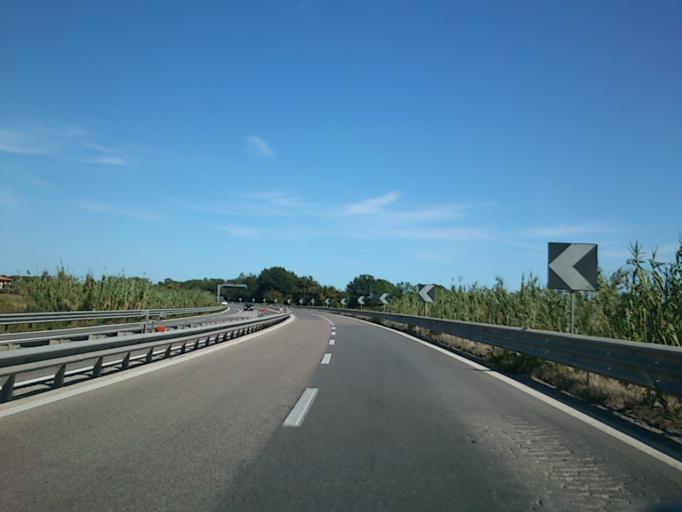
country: IT
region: The Marches
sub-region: Provincia di Pesaro e Urbino
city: Bellocchi
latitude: 43.8060
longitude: 13.0169
